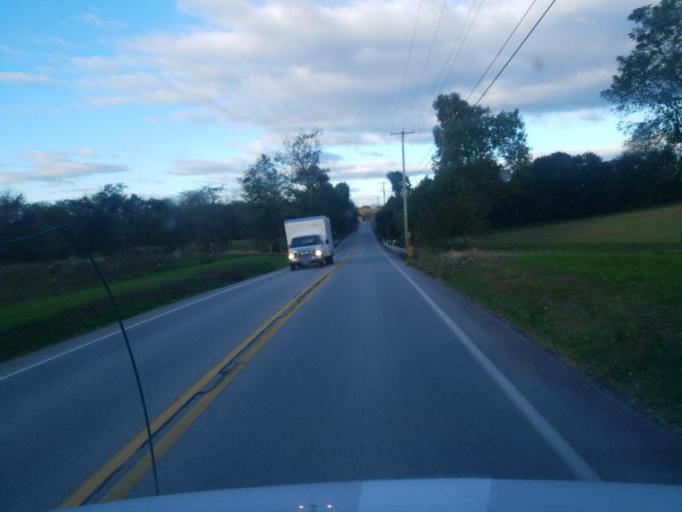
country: US
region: Pennsylvania
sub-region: Adams County
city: East Berlin
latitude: 39.9372
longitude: -77.0224
